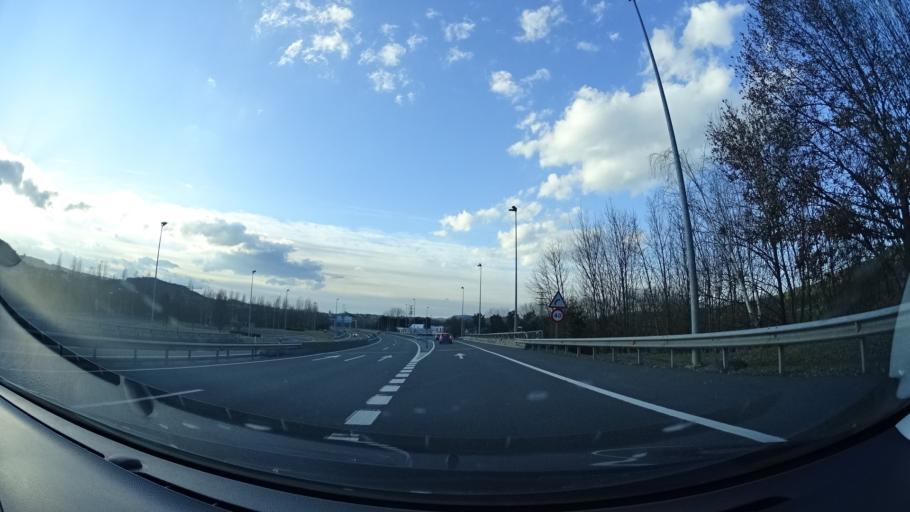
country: ES
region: Basque Country
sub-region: Bizkaia
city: Mungia
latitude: 43.3598
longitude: -2.8431
